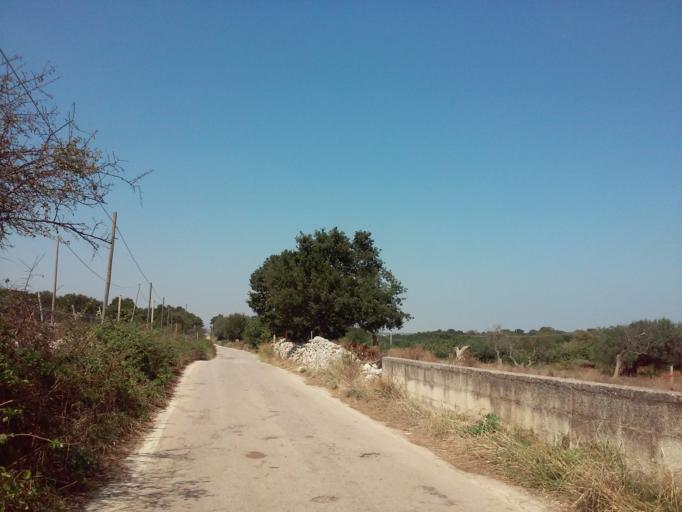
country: IT
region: Apulia
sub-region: Provincia di Bari
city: Alberobello
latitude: 40.7998
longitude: 17.2131
